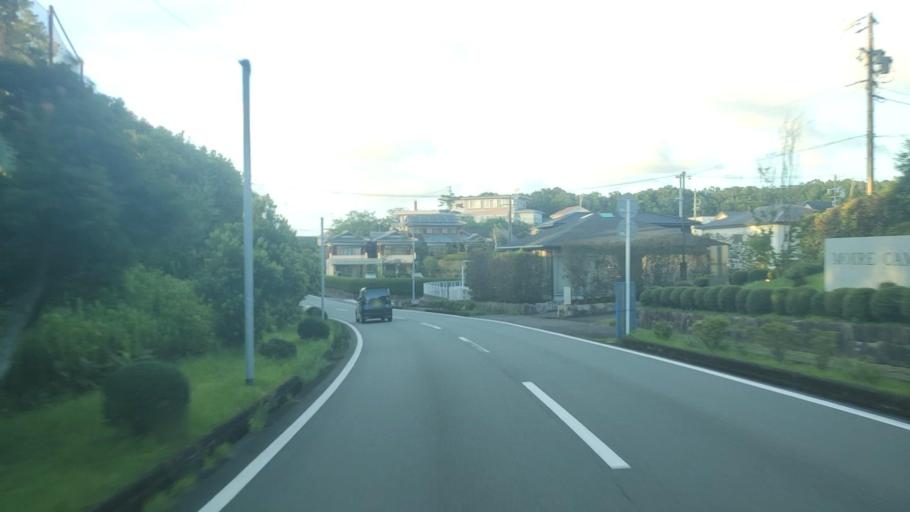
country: JP
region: Mie
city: Toba
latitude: 34.3228
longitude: 136.8214
